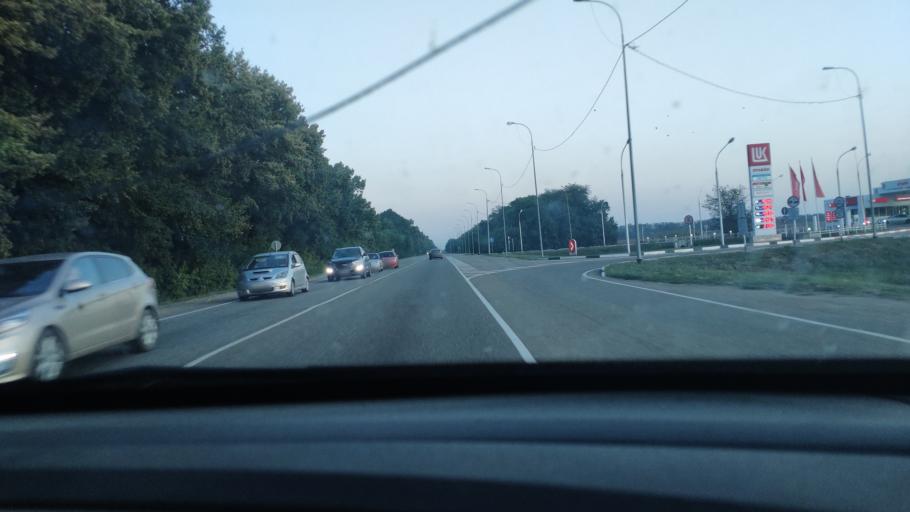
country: RU
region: Krasnodarskiy
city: Medvedovskaya
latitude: 45.4461
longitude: 38.9937
